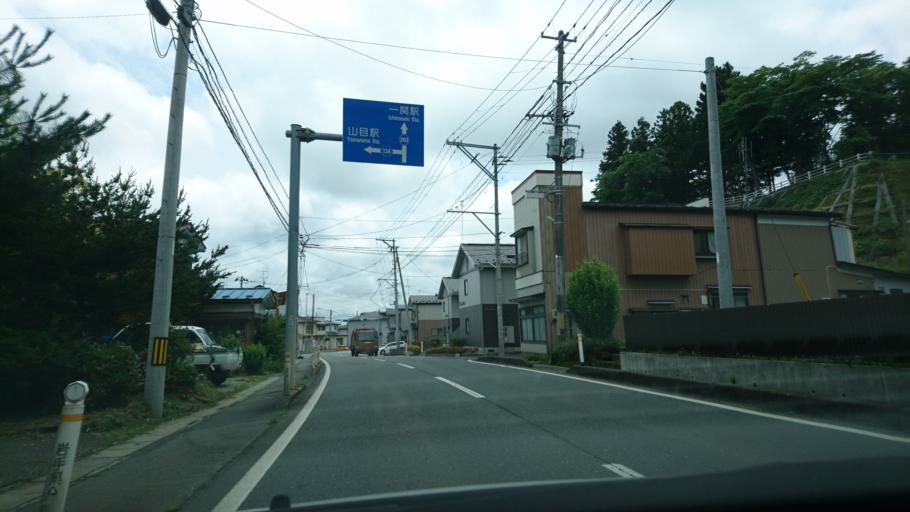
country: JP
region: Iwate
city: Ichinoseki
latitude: 38.9519
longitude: 141.1305
